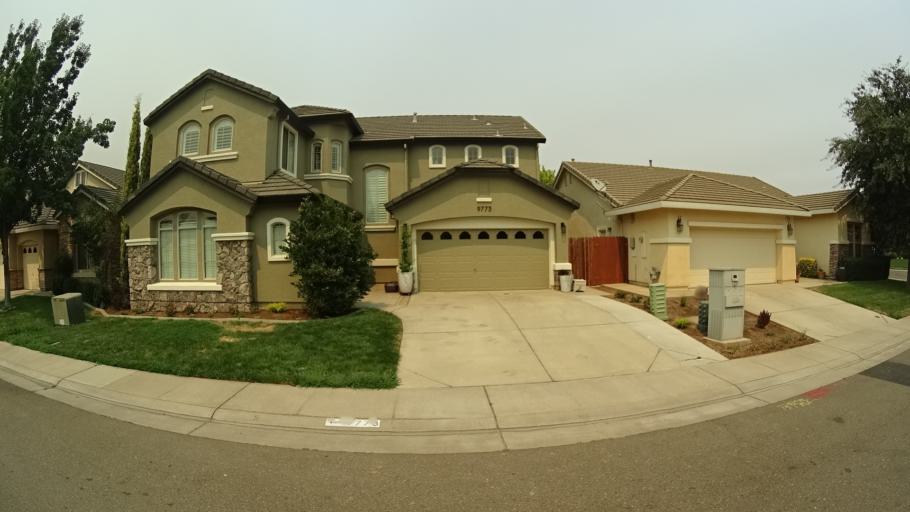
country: US
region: California
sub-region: Sacramento County
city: Laguna
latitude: 38.4035
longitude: -121.4231
